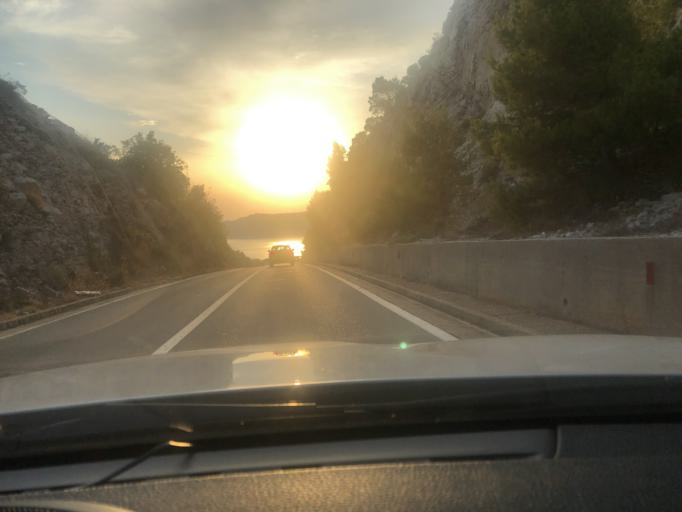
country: HR
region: Splitsko-Dalmatinska
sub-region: Grad Hvar
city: Hvar
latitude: 43.1527
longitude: 16.5133
